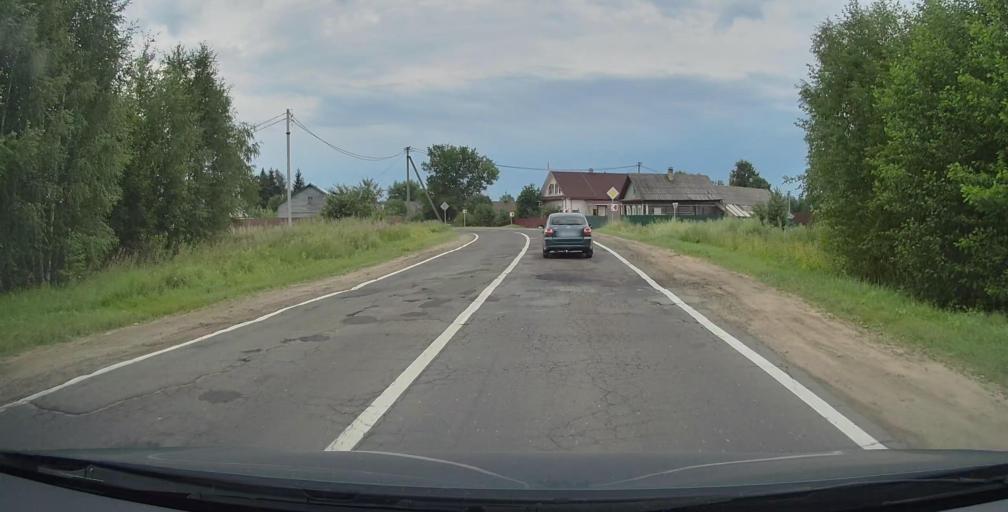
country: RU
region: Jaroslavl
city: Myshkin
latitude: 57.8677
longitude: 38.5048
